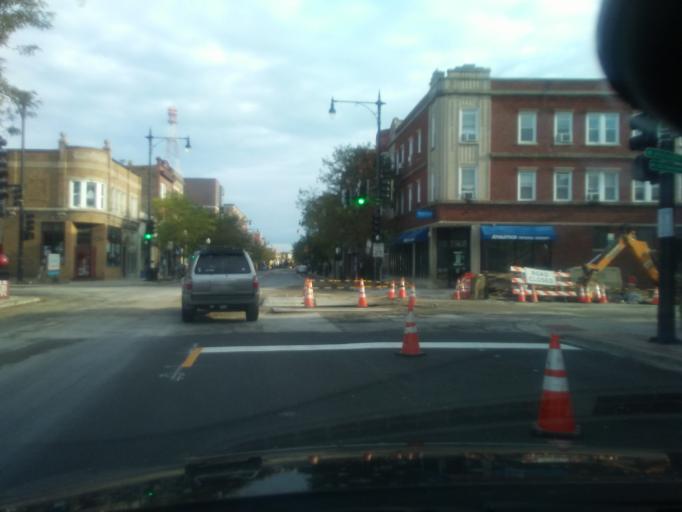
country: US
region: Illinois
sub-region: Cook County
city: Lincolnwood
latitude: 41.9732
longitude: -87.6681
